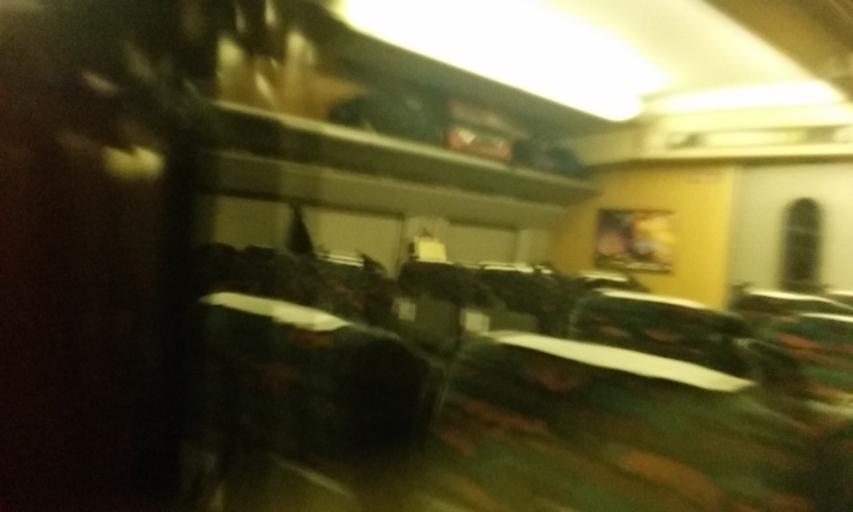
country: JP
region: Miyagi
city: Okawara
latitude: 38.1020
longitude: 140.7688
